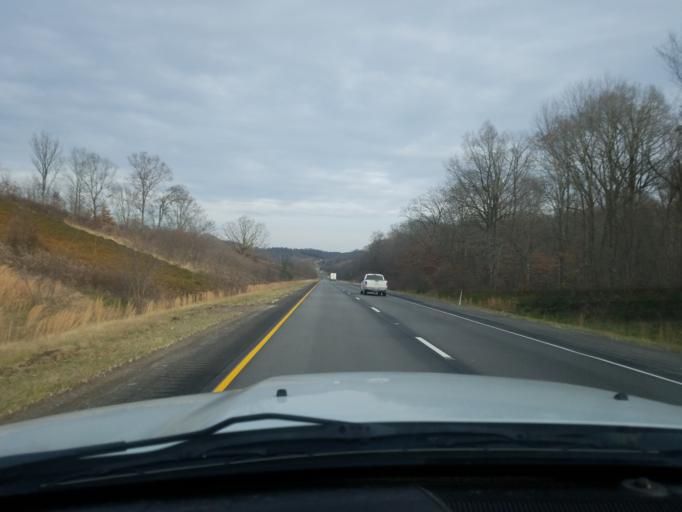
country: US
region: Indiana
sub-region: Dubois County
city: Ferdinand
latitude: 38.2039
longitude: -86.8175
